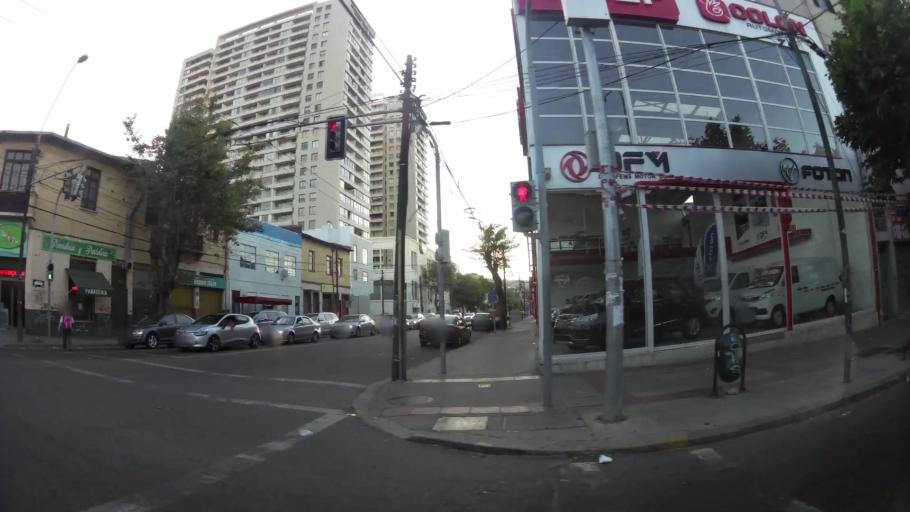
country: CL
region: Valparaiso
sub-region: Provincia de Valparaiso
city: Valparaiso
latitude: -33.0504
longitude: -71.6085
